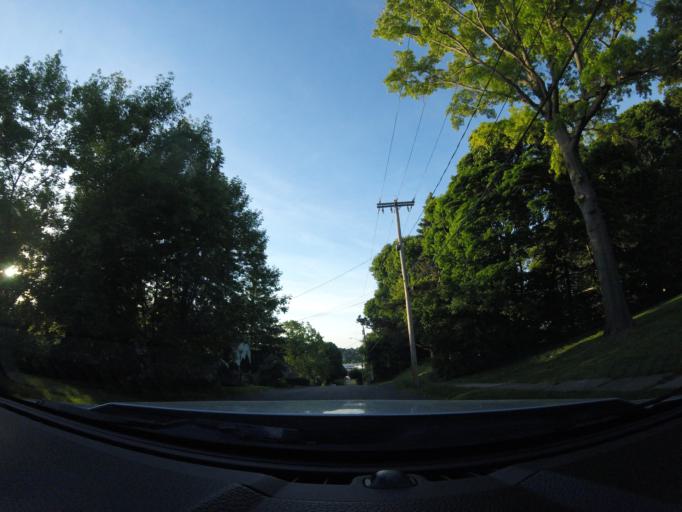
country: US
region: New York
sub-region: Onondaga County
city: East Syracuse
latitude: 43.0494
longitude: -76.1083
